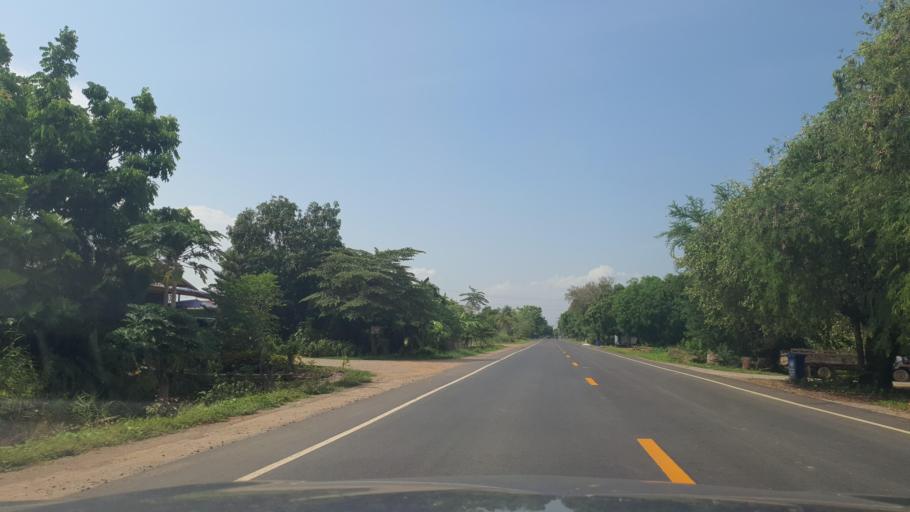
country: TH
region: Sukhothai
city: Si Samrong
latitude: 17.1530
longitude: 99.8260
